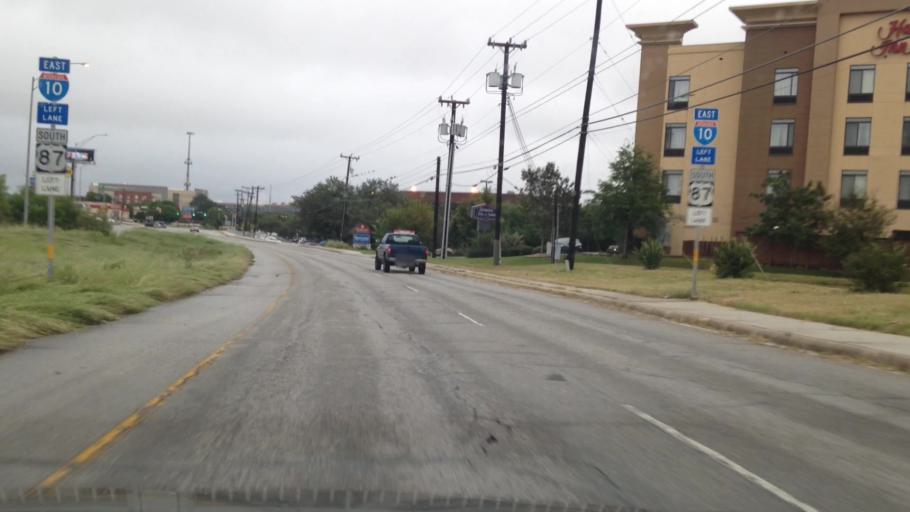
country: US
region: Texas
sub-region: Bexar County
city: Shavano Park
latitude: 29.5484
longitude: -98.5855
